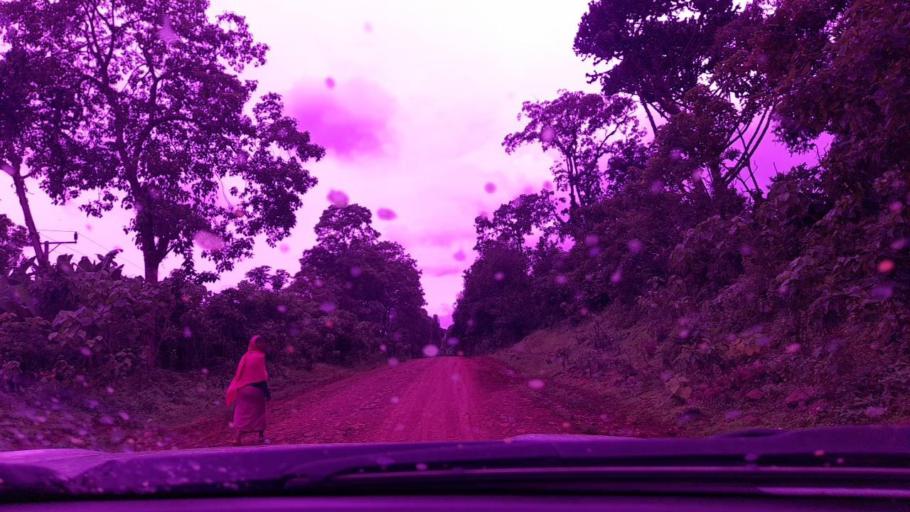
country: ET
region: Southern Nations, Nationalities, and People's Region
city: Tippi
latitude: 7.5717
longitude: 35.6476
